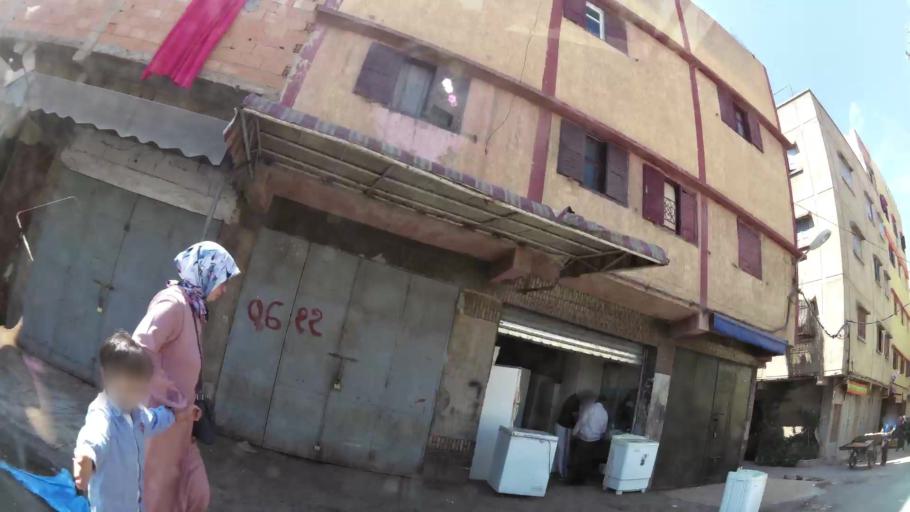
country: MA
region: Rabat-Sale-Zemmour-Zaer
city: Sale
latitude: 34.0626
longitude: -6.7778
